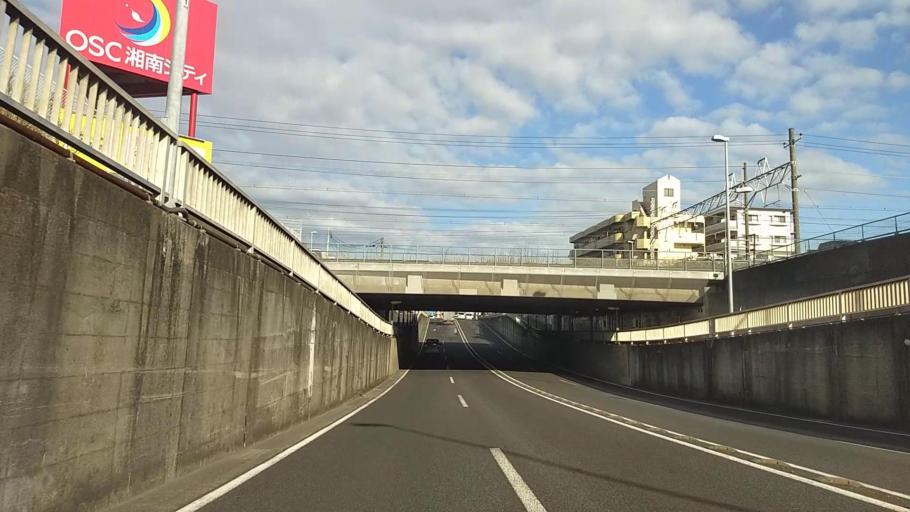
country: JP
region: Kanagawa
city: Hiratsuka
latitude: 35.3290
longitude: 139.3597
